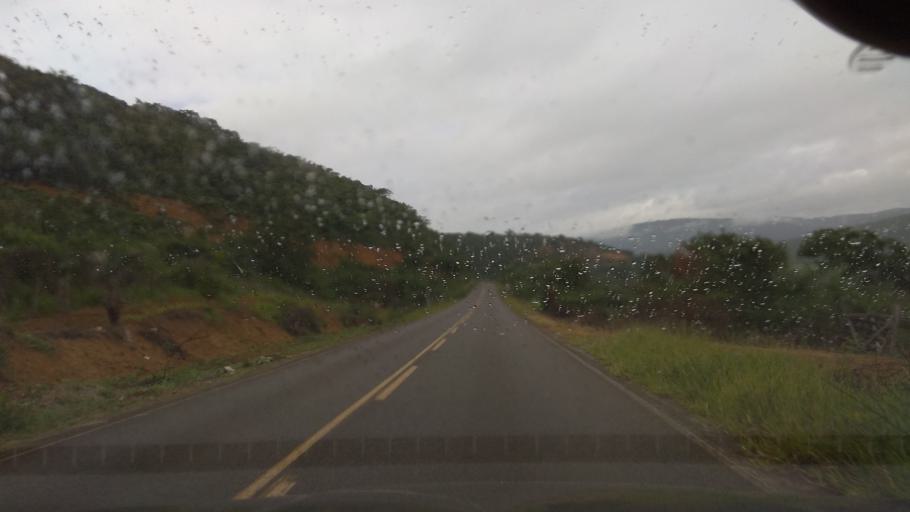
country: BR
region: Bahia
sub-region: Ubaira
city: Ubaira
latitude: -13.2393
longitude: -39.7391
